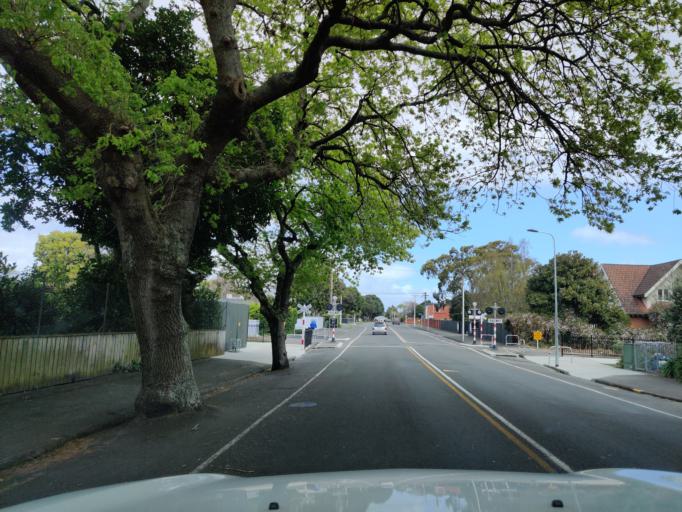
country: NZ
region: Manawatu-Wanganui
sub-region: Wanganui District
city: Wanganui
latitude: -39.9282
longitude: 175.0401
